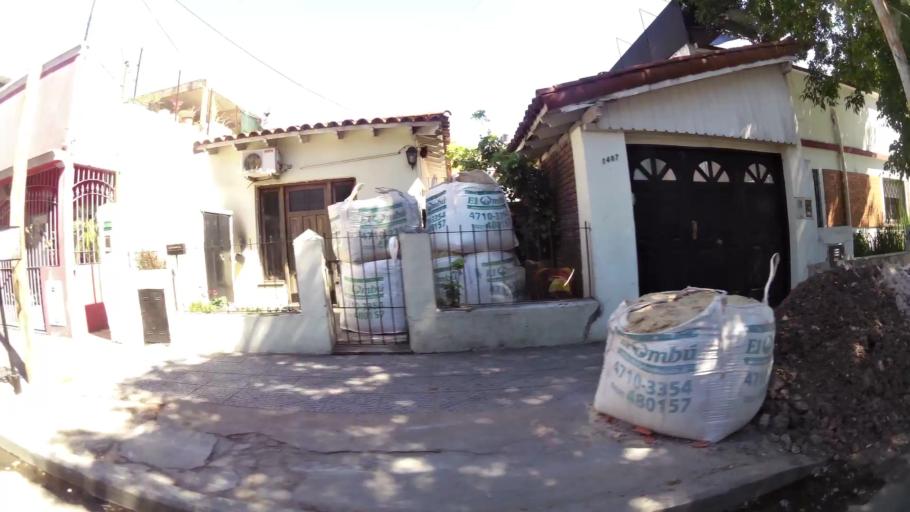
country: AR
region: Buenos Aires
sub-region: Partido de General San Martin
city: General San Martin
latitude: -34.5259
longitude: -58.5298
